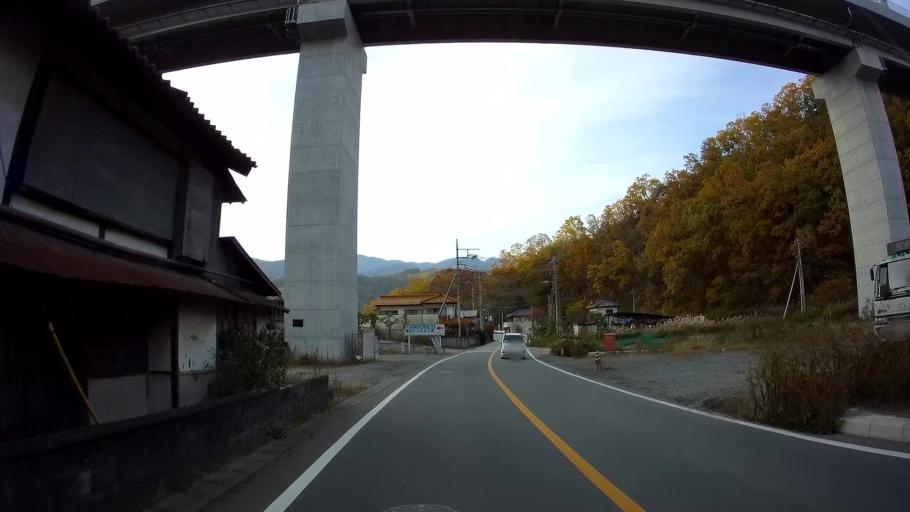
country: JP
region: Yamanashi
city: Ryuo
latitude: 35.4817
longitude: 138.4596
